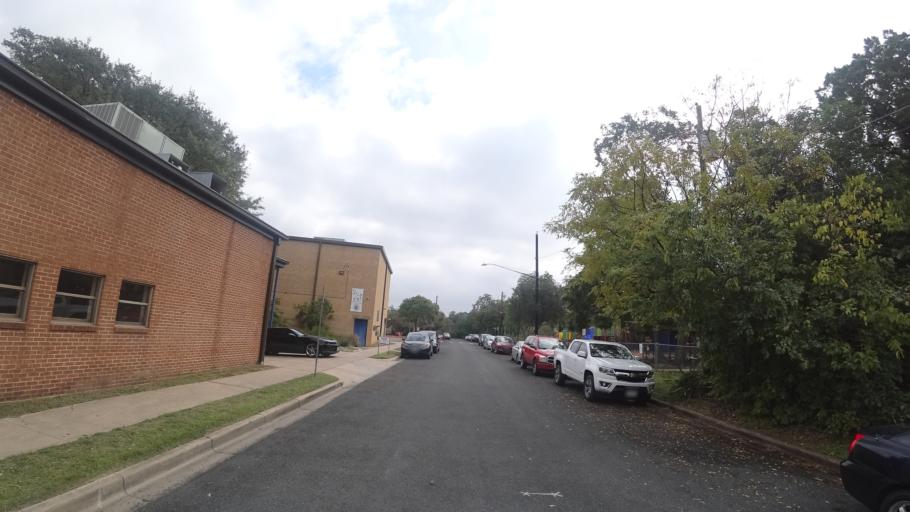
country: US
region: Texas
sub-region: Travis County
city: Austin
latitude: 30.2505
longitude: -97.7605
